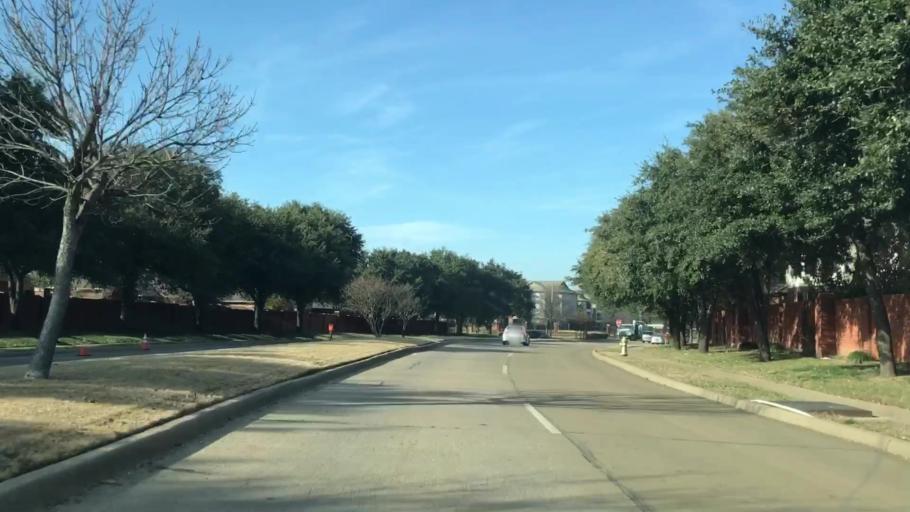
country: US
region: Texas
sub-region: Dallas County
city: Farmers Branch
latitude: 32.9259
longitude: -96.9453
